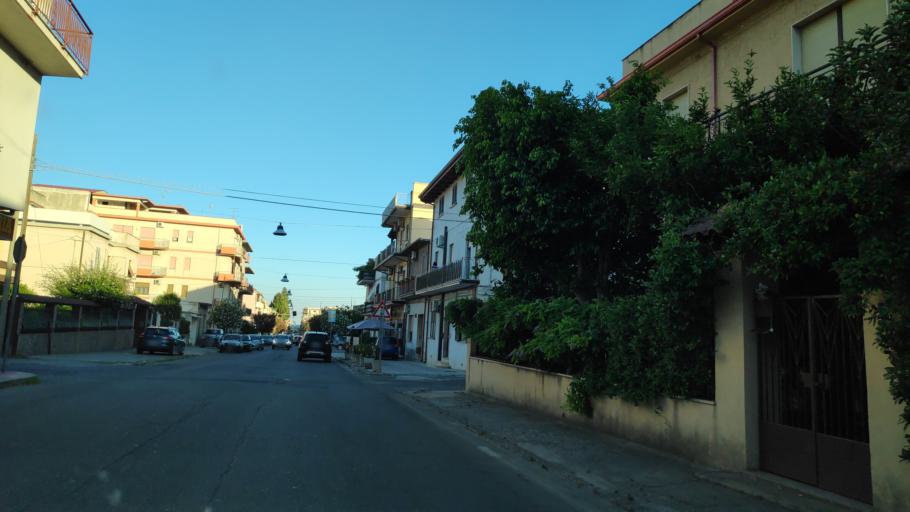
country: IT
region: Calabria
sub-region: Provincia di Reggio Calabria
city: Locri
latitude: 38.2375
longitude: 16.2576
